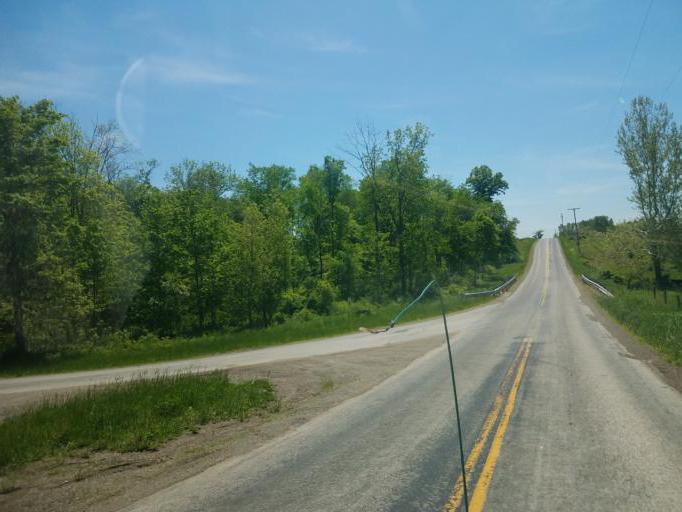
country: US
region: Ohio
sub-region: Ashland County
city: Ashland
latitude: 40.9449
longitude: -82.2436
